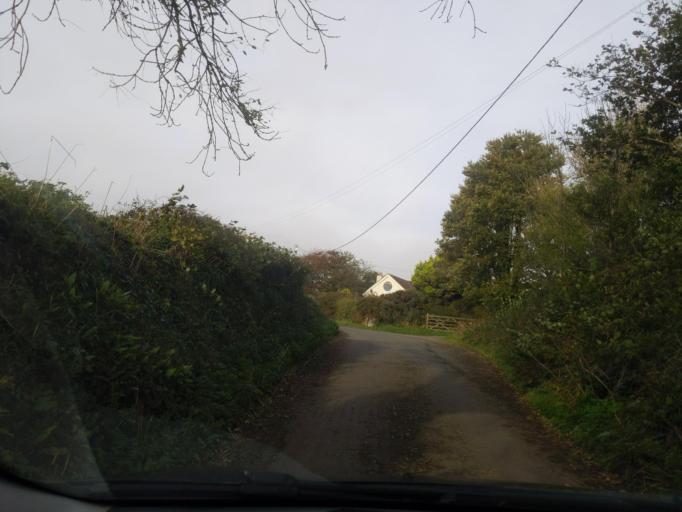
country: GB
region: England
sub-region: Cornwall
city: Looe
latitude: 50.3712
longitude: -4.4163
